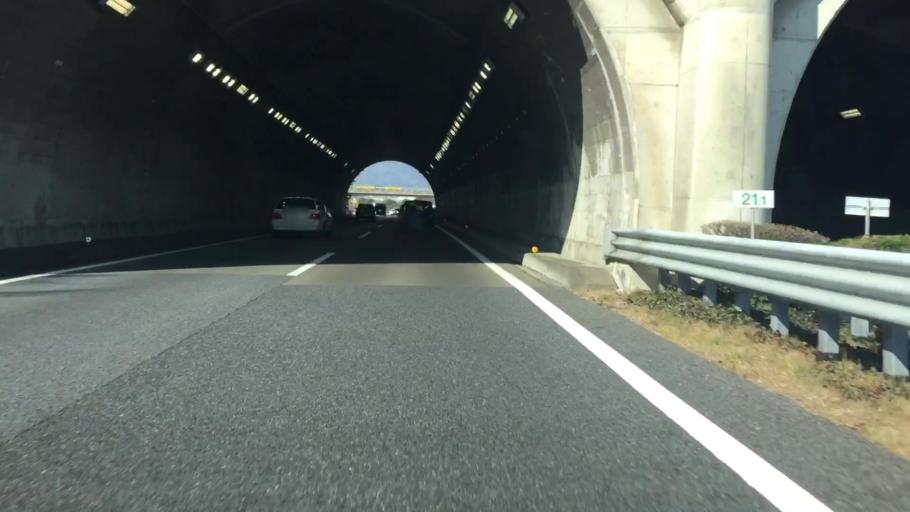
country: JP
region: Gunma
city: Tomioka
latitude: 36.2405
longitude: 138.8842
